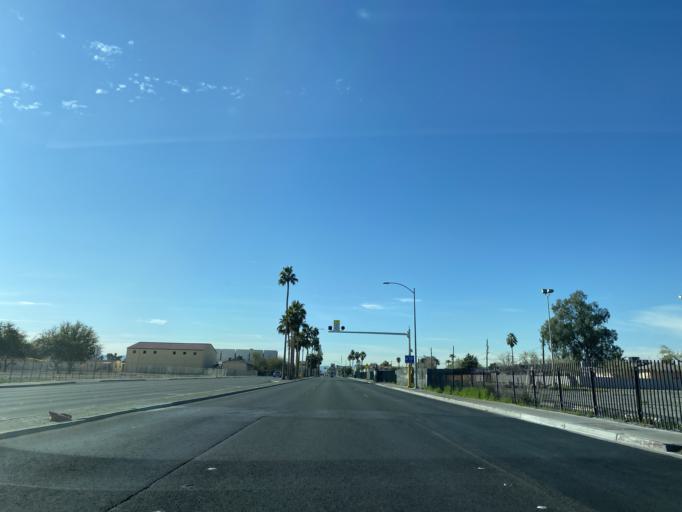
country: US
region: Nevada
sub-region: Clark County
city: Las Vegas
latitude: 36.1516
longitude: -115.1371
